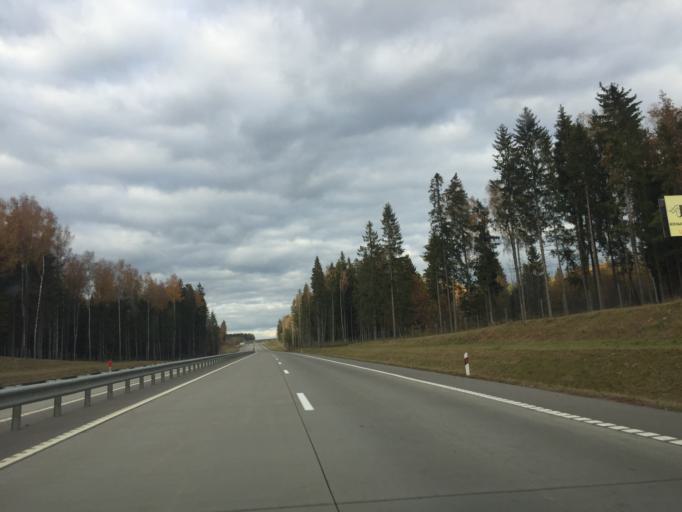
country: BY
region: Minsk
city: Rakaw
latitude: 54.0103
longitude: 27.1331
